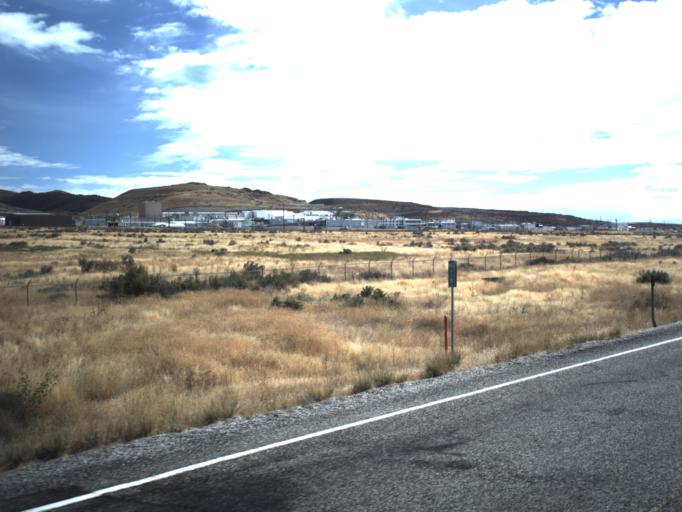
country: US
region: Utah
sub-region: Box Elder County
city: Tremonton
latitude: 41.6681
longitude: -112.4459
